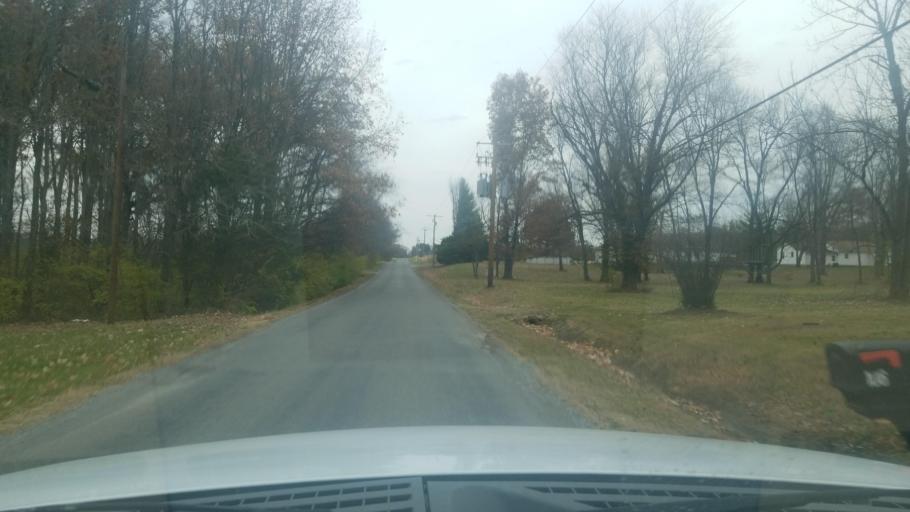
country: US
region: Illinois
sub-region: Saline County
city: Harrisburg
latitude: 37.7416
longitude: -88.5681
